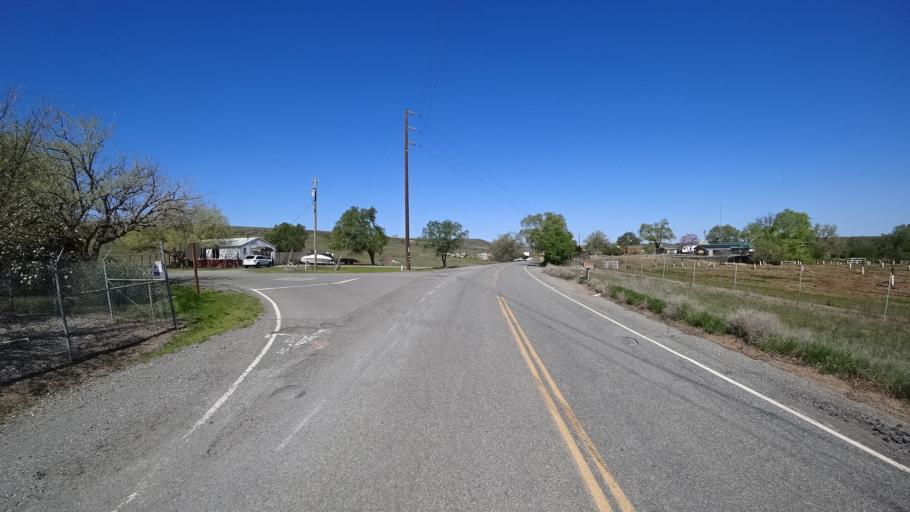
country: US
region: California
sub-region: Glenn County
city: Orland
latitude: 39.8069
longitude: -122.3300
